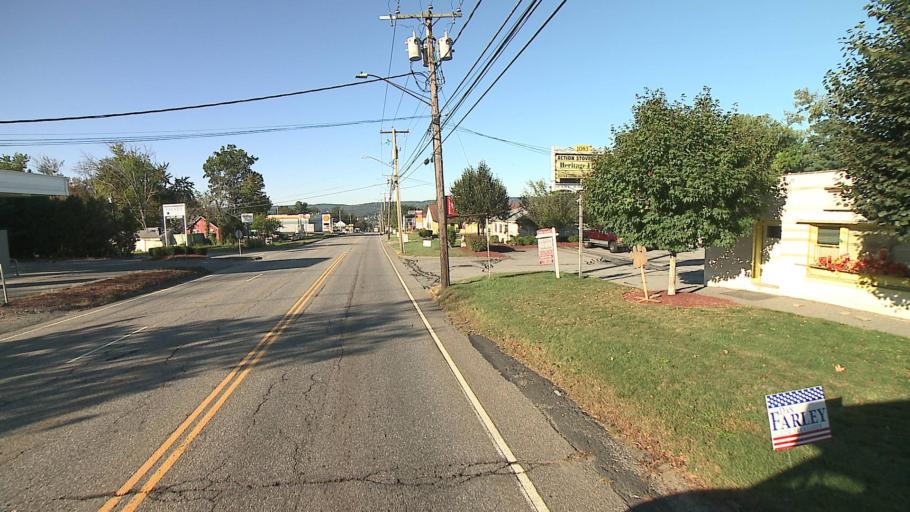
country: US
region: Connecticut
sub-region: Litchfield County
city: Torrington
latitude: 41.8143
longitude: -73.0973
